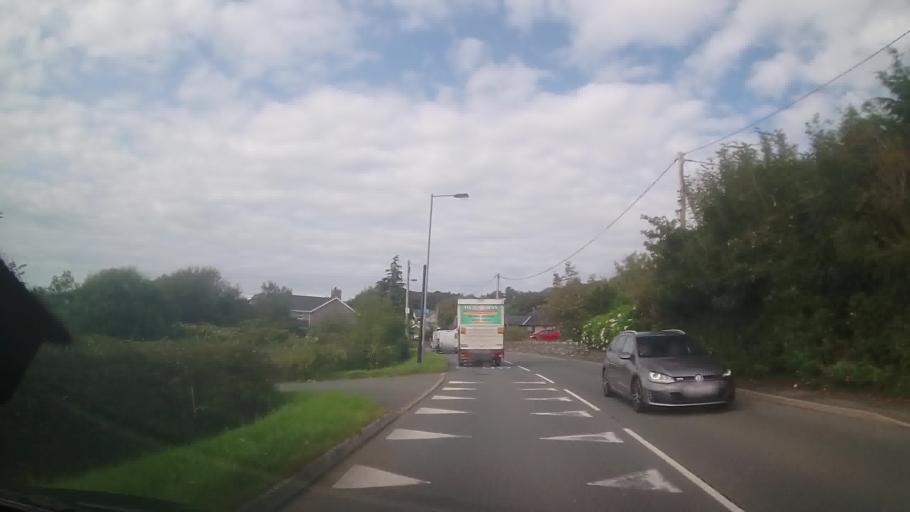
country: GB
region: Wales
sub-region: Gwynedd
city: Dyffryn Ardudwy
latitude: 52.7838
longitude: -4.0967
